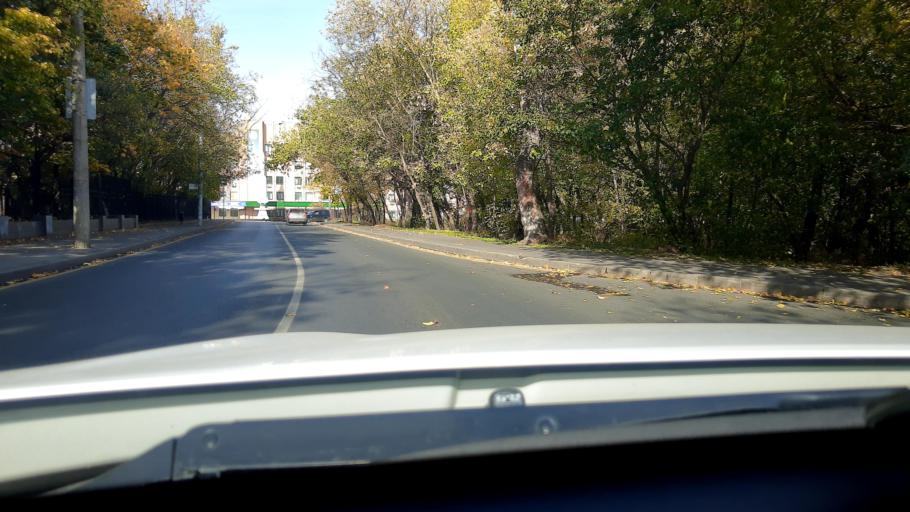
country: RU
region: Moskovskaya
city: Fili
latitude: 55.7519
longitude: 37.4937
